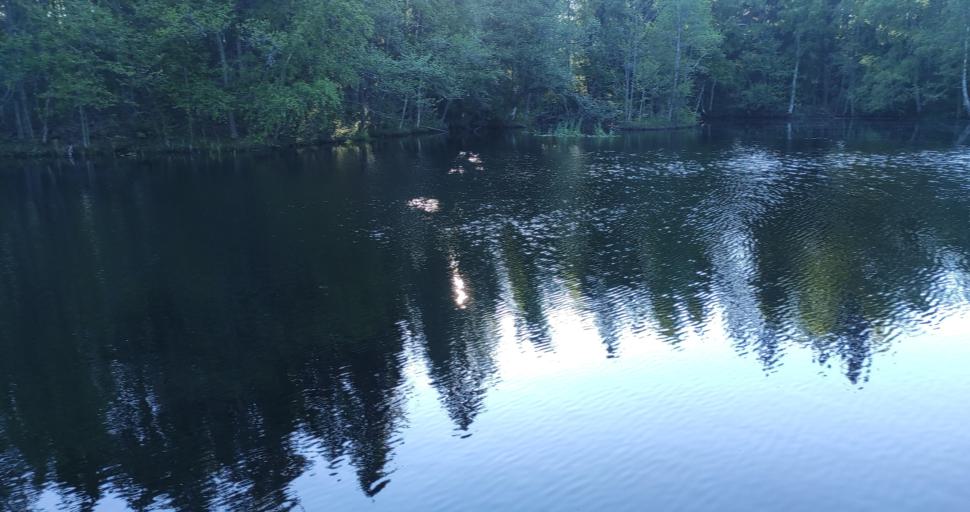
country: RU
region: Leningrad
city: Vysotsk
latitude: 60.5911
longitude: 28.3260
